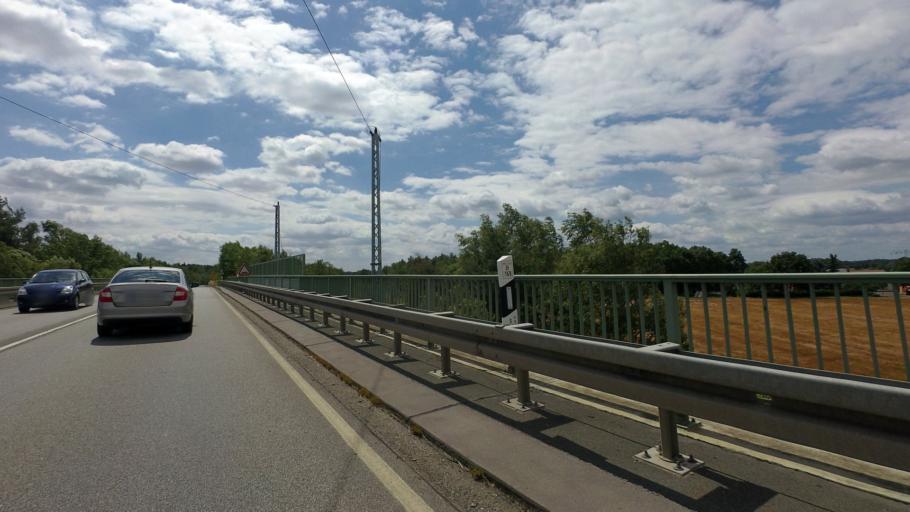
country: DE
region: Brandenburg
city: Grossraschen
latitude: 51.5746
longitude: 14.0801
